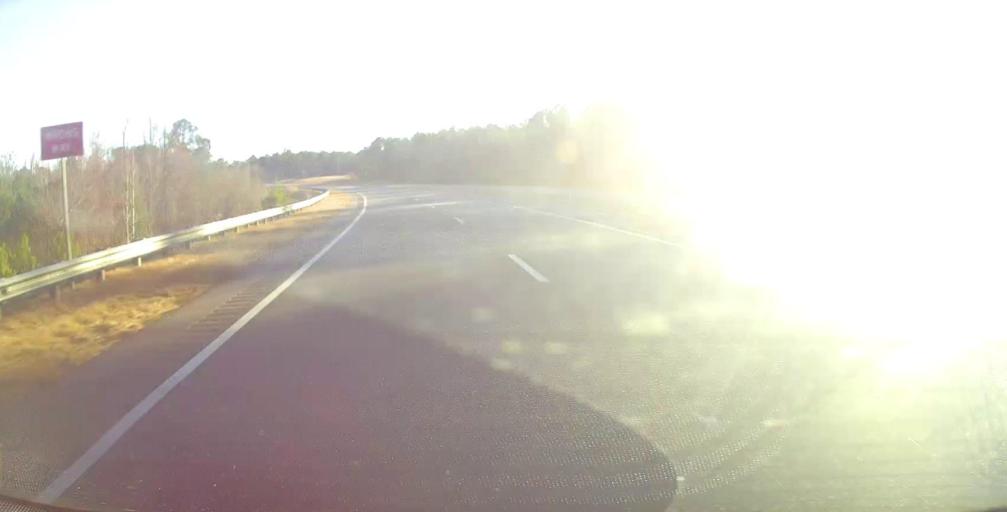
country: US
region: Georgia
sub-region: Upson County
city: Thomaston
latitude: 32.7747
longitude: -84.2464
